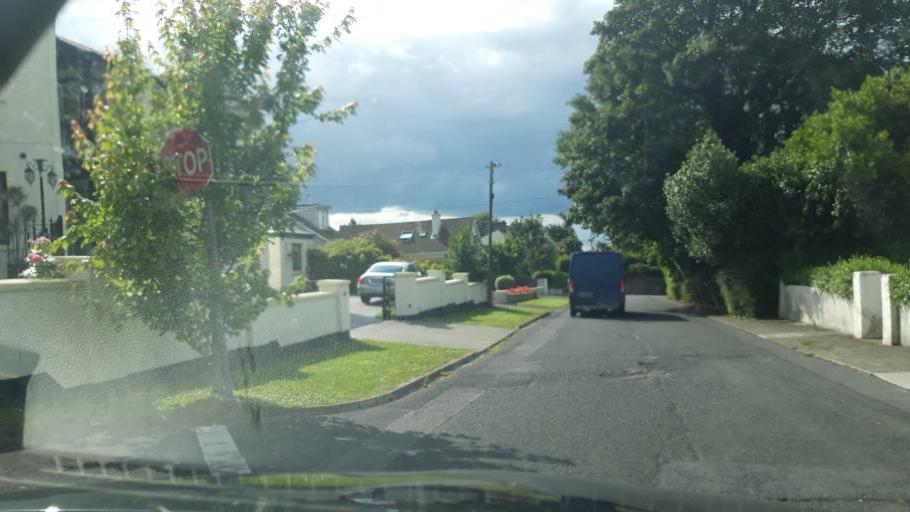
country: IE
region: Munster
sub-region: Waterford
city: Waterford
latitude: 52.2473
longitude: -7.0965
